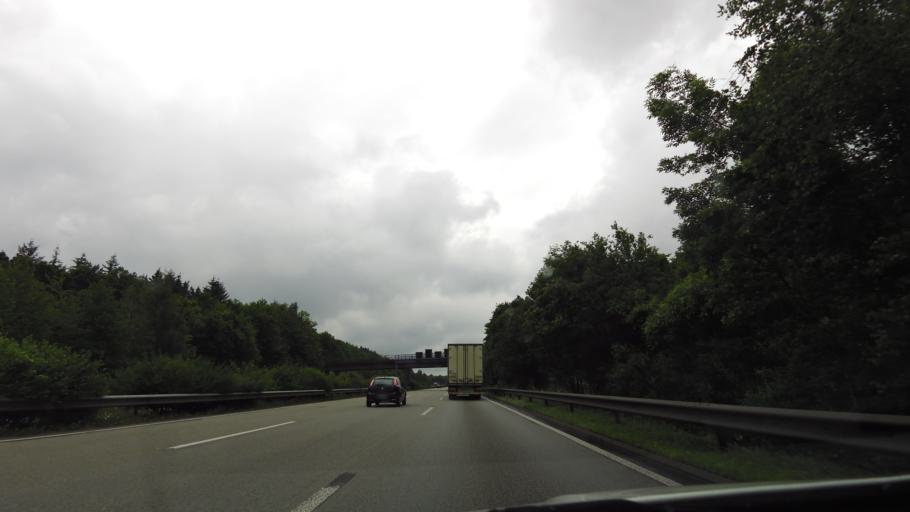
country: DE
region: Rheinland-Pfalz
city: Konigsfeld
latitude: 50.5322
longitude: 7.1785
